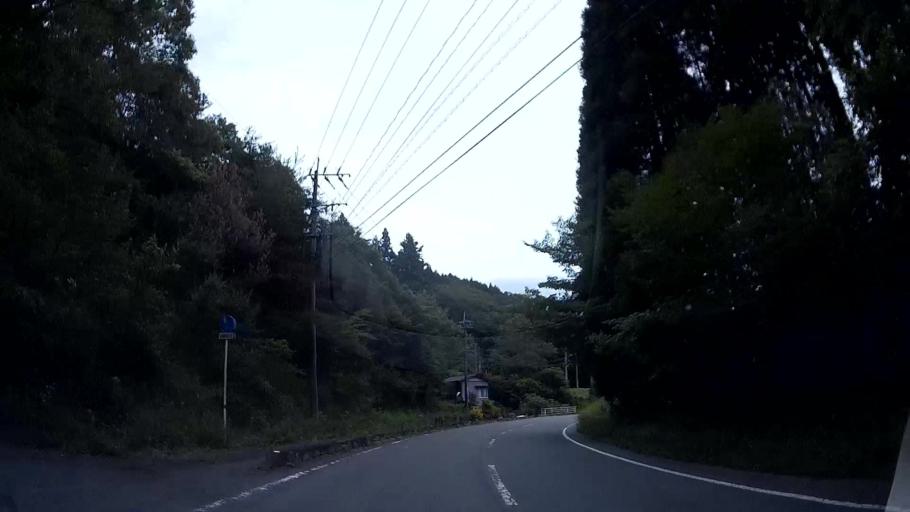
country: JP
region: Oita
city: Hita
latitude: 33.1300
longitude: 130.9949
